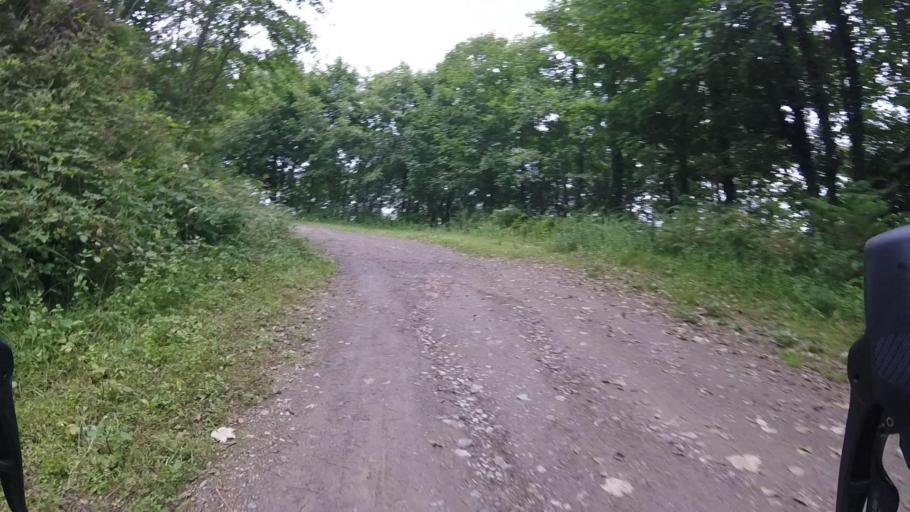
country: ES
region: Navarre
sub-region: Provincia de Navarra
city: Arano
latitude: 43.2544
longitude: -1.8890
